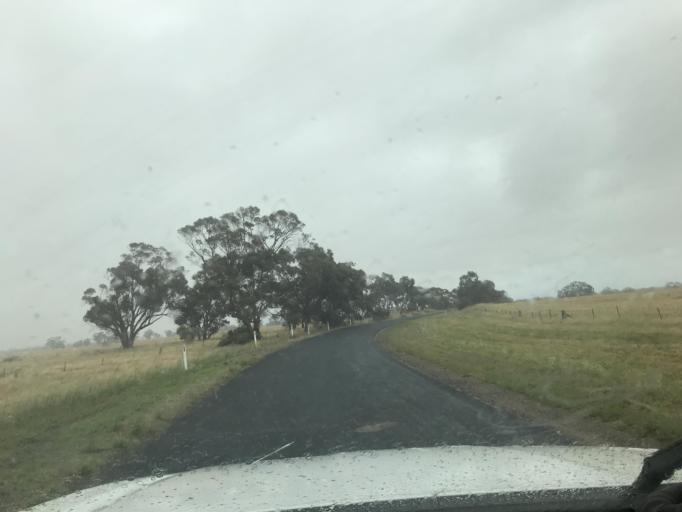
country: AU
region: South Australia
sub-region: Tatiara
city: Bordertown
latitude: -36.3263
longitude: 141.2077
